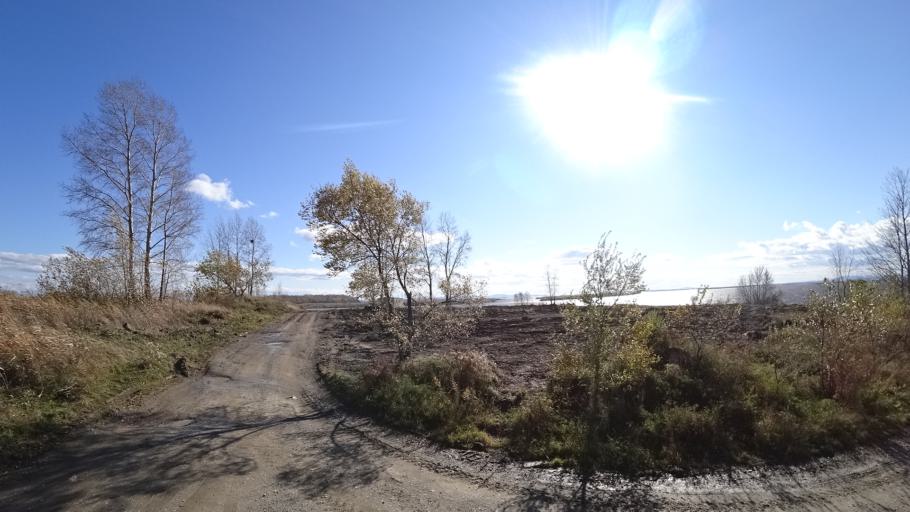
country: RU
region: Khabarovsk Krai
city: Amursk
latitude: 50.2155
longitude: 136.8888
